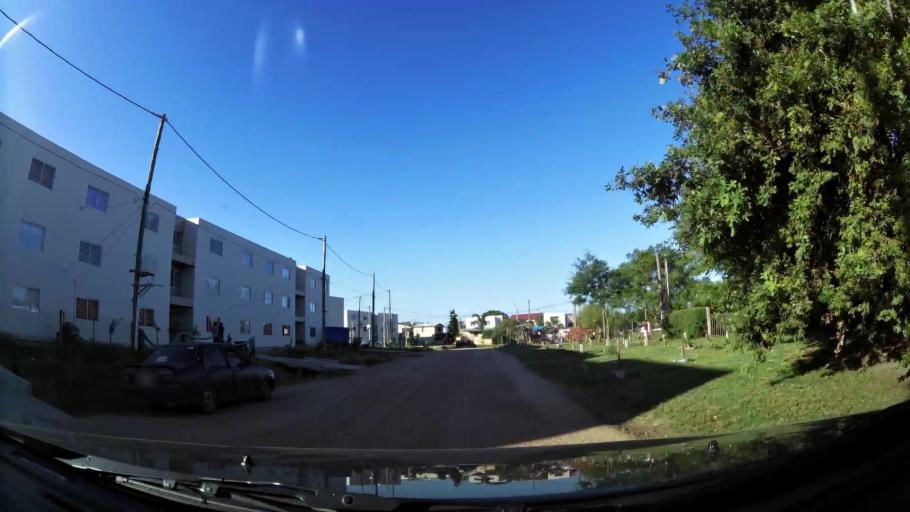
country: UY
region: Canelones
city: Paso de Carrasco
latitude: -34.8536
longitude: -56.0530
